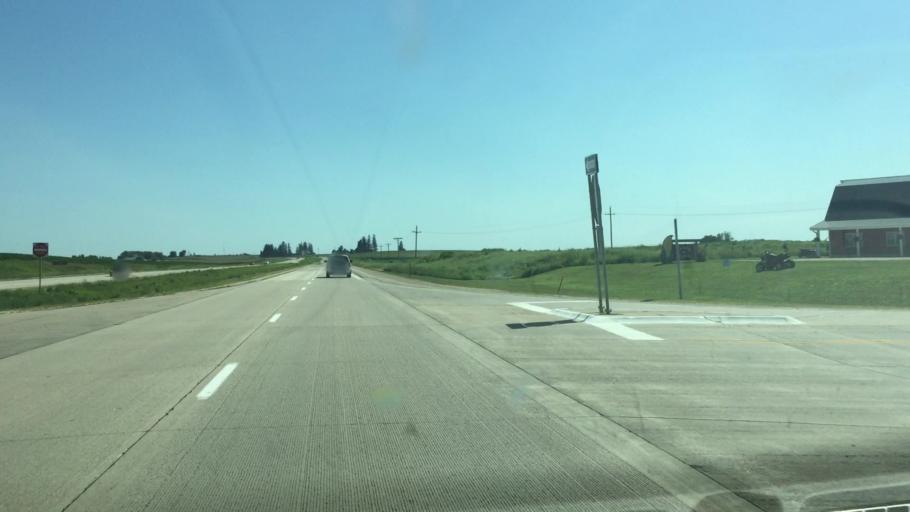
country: US
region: Iowa
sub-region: Jones County
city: Monticello
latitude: 42.1843
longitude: -91.2216
